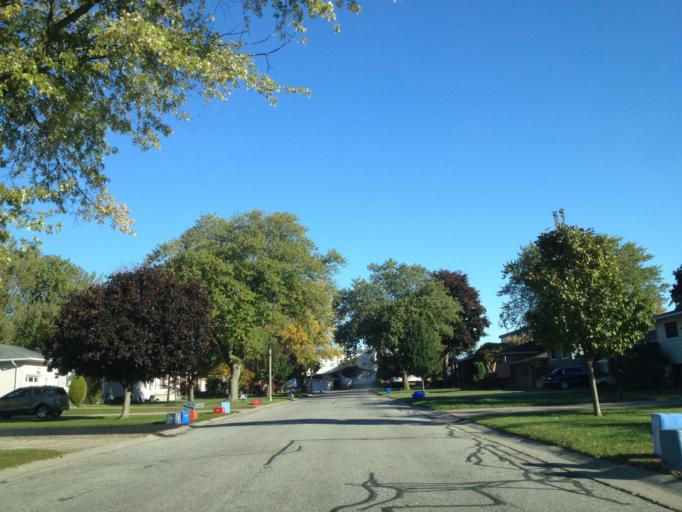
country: CA
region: Ontario
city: Amherstburg
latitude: 42.0301
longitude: -82.5970
